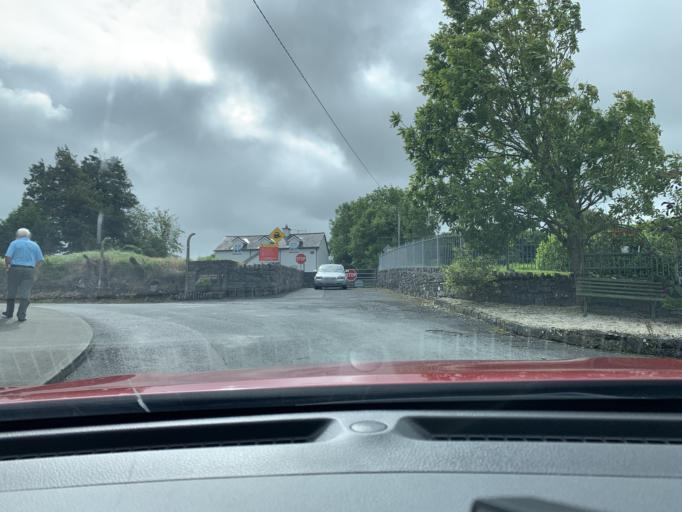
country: IE
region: Connaught
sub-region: Roscommon
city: Boyle
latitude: 53.9689
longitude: -8.2978
